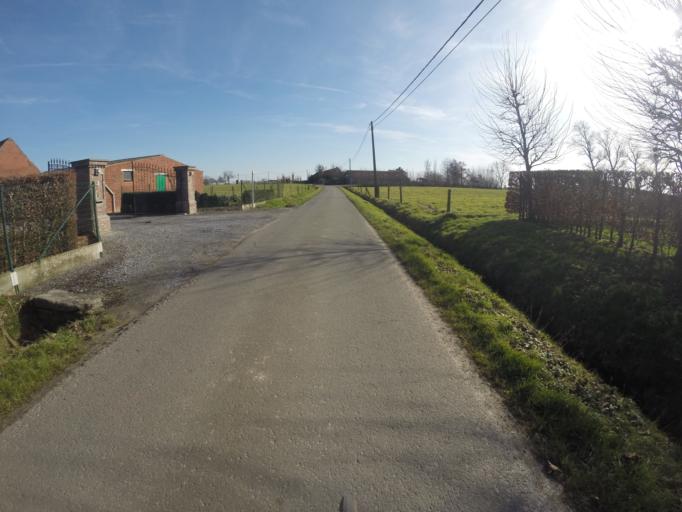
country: BE
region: Flanders
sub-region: Provincie West-Vlaanderen
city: Ruiselede
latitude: 51.0498
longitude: 3.3511
